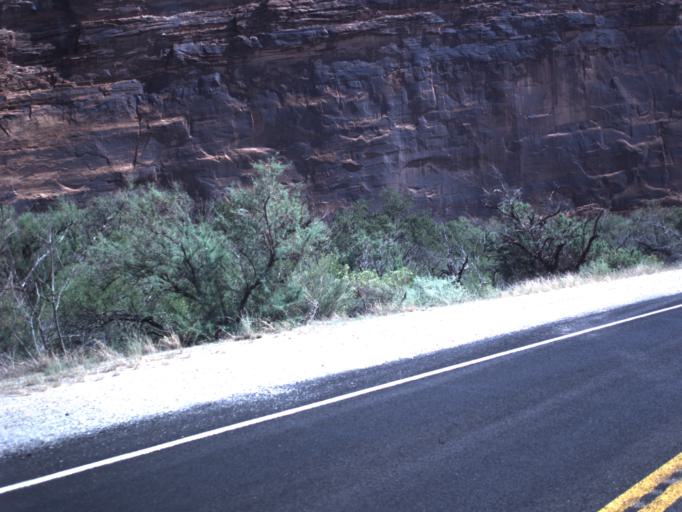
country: US
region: Utah
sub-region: Grand County
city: Moab
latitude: 38.5494
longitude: -109.6474
